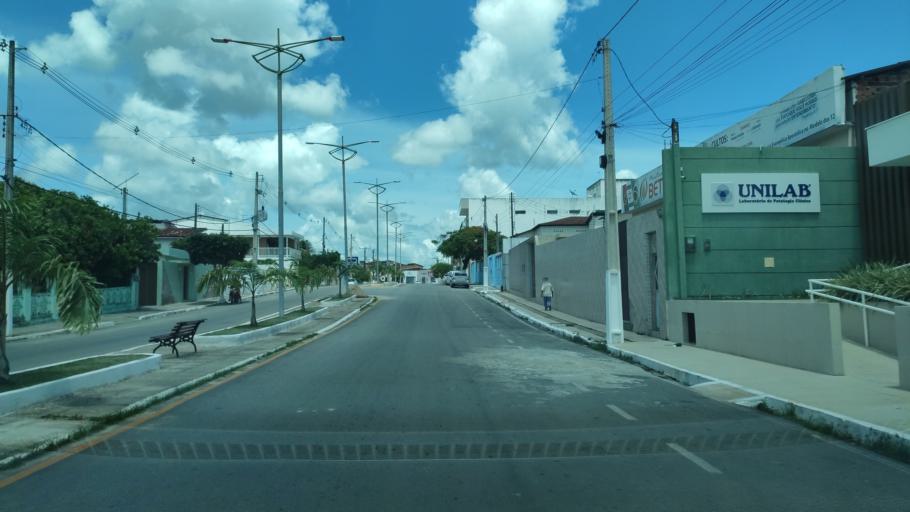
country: BR
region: Alagoas
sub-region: Uniao Dos Palmares
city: Uniao dos Palmares
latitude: -9.1613
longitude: -36.0322
